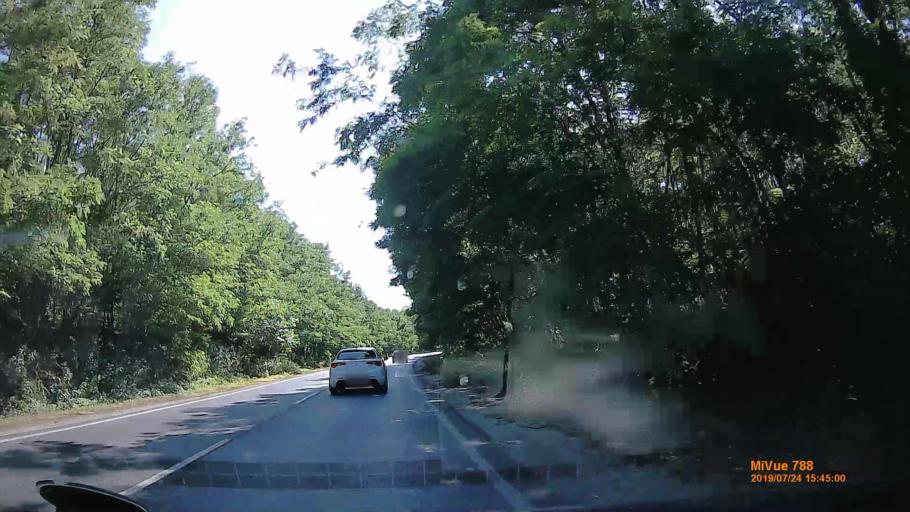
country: HU
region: Szabolcs-Szatmar-Bereg
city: Nagydobos
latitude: 48.0934
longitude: 22.2869
